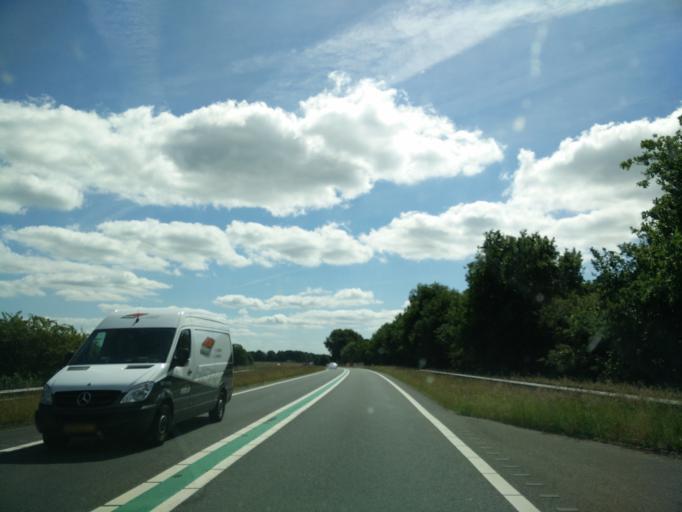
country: NL
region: Drenthe
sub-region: Gemeente Coevorden
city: Sleen
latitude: 52.8059
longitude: 6.7018
